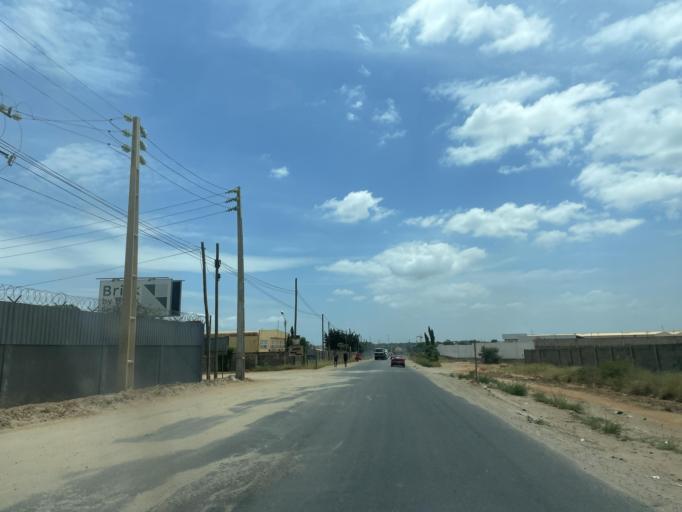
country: AO
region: Luanda
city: Luanda
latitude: -8.9408
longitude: 13.3874
